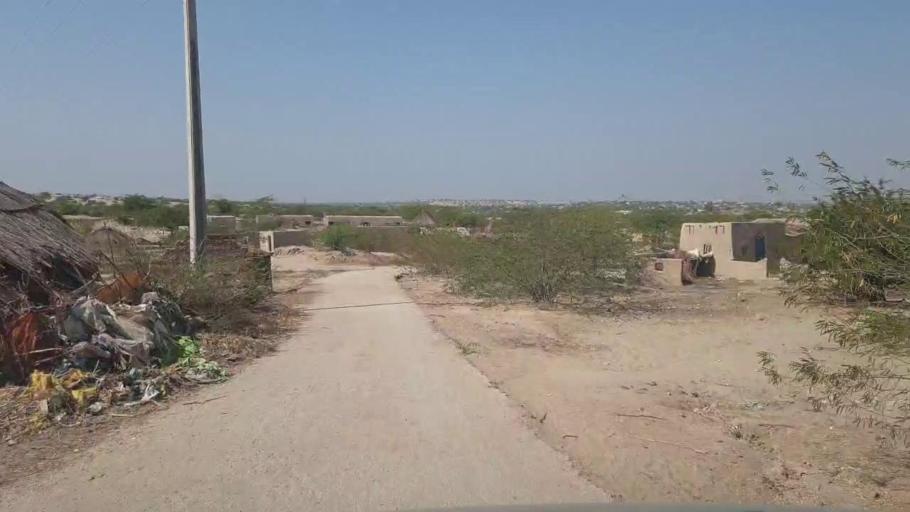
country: PK
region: Sindh
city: Dhoro Naro
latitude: 25.5157
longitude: 69.5622
